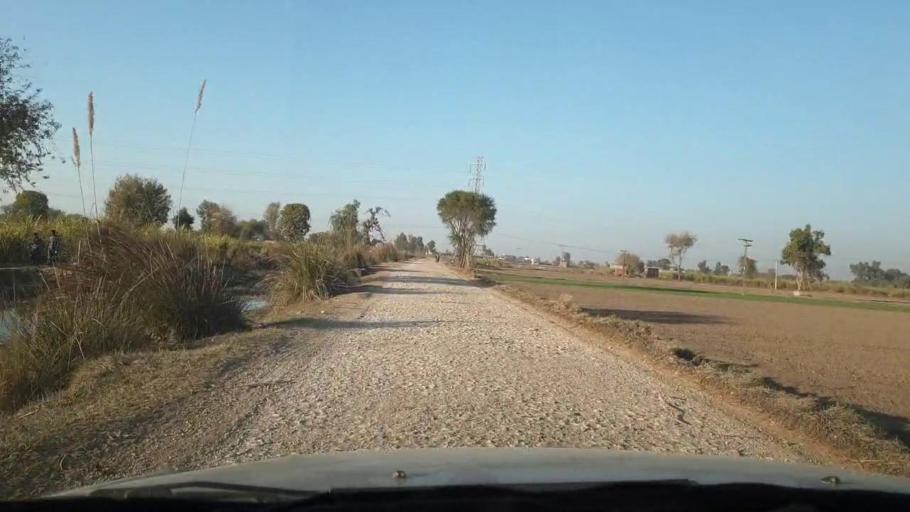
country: PK
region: Sindh
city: Ghotki
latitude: 27.9896
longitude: 69.2728
